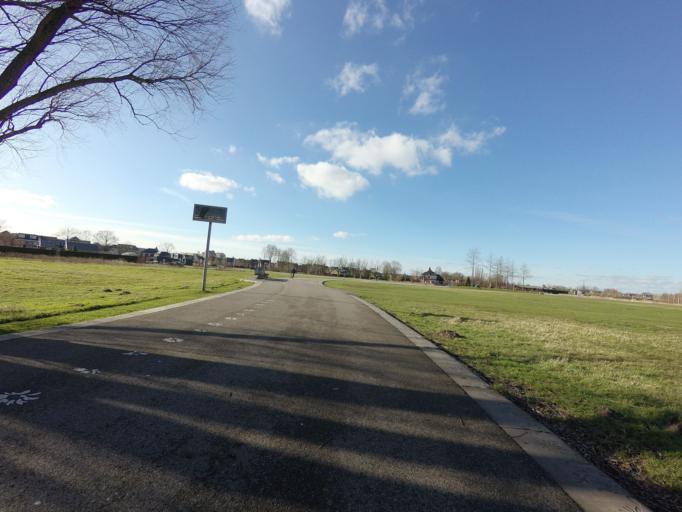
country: NL
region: Utrecht
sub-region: Stichtse Vecht
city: Spechtenkamp
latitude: 52.0943
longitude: 5.0216
